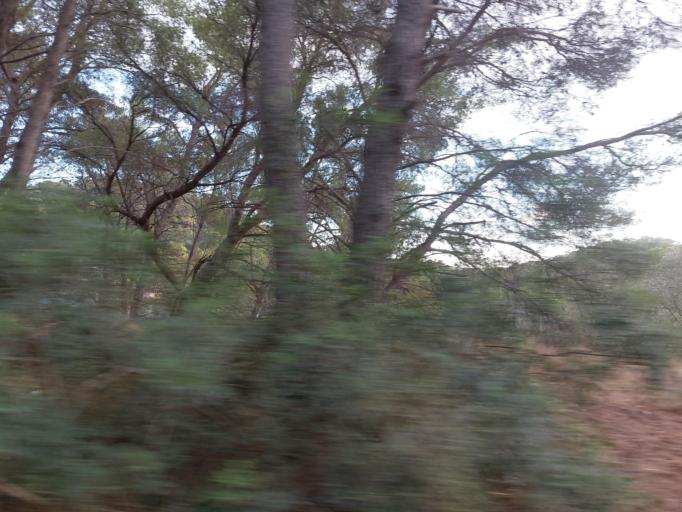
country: HR
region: Dubrovacko-Neretvanska
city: Smokvica
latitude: 42.7660
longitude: 16.8126
